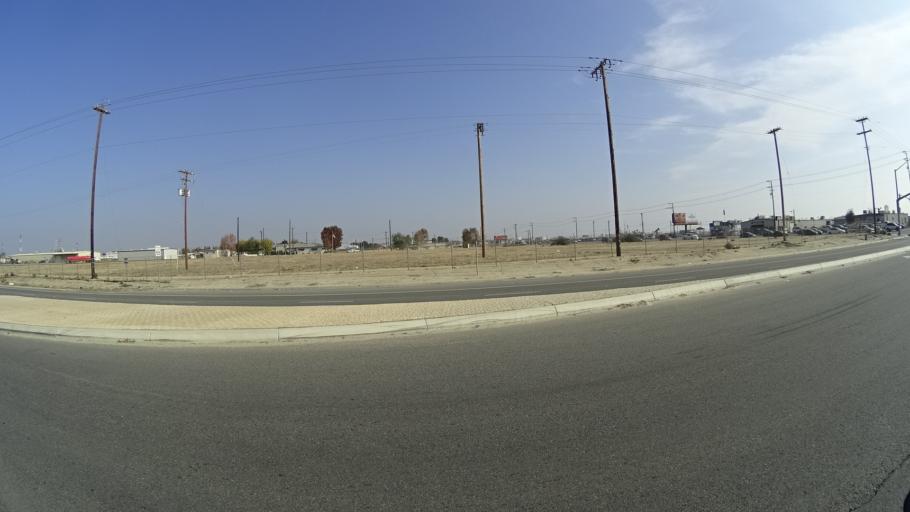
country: US
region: California
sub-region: Kern County
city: Greenacres
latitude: 35.3843
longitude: -119.0655
